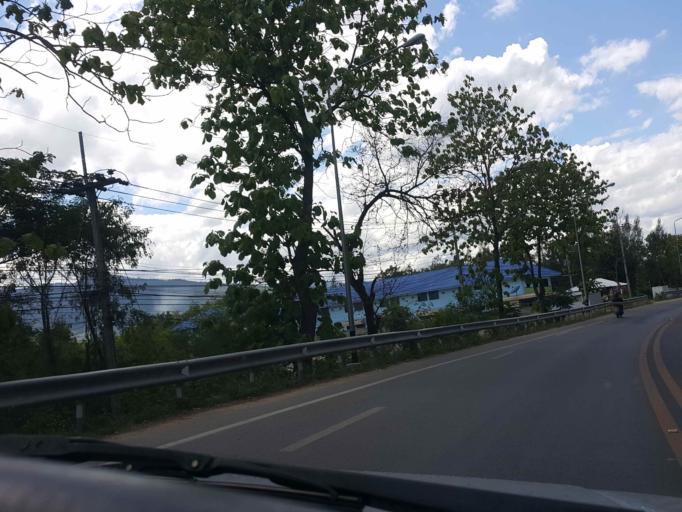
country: TH
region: Chiang Mai
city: Chom Thong
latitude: 18.4519
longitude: 98.6737
